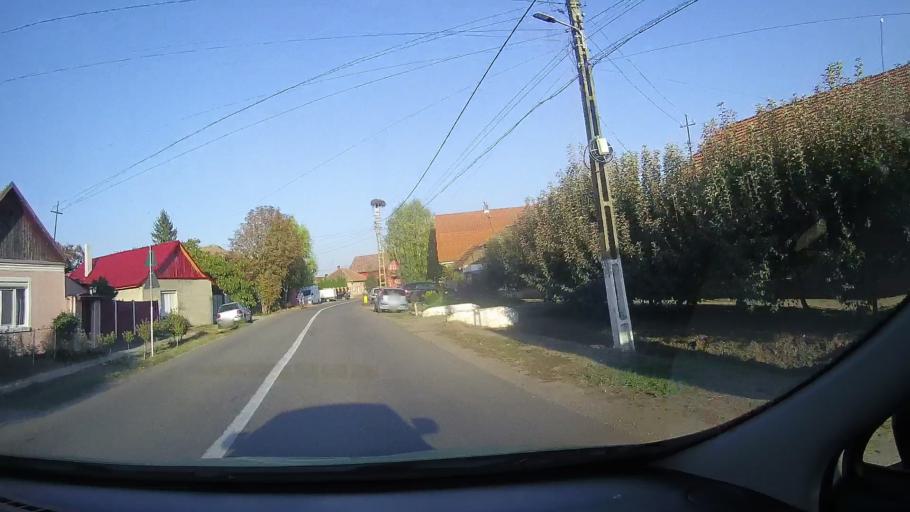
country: RO
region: Bihor
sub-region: Comuna Bors
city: Bors
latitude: 47.1155
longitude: 21.8233
